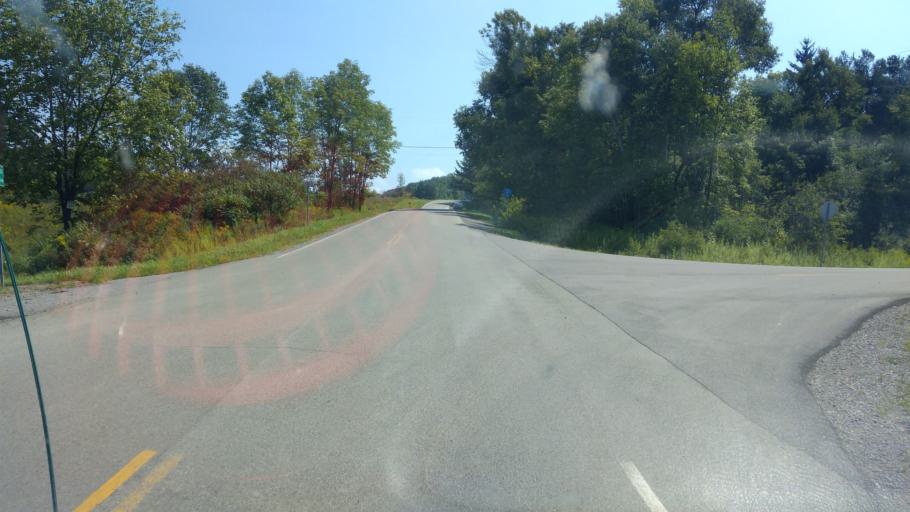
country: US
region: New York
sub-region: Allegany County
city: Belmont
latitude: 42.2923
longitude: -77.9391
